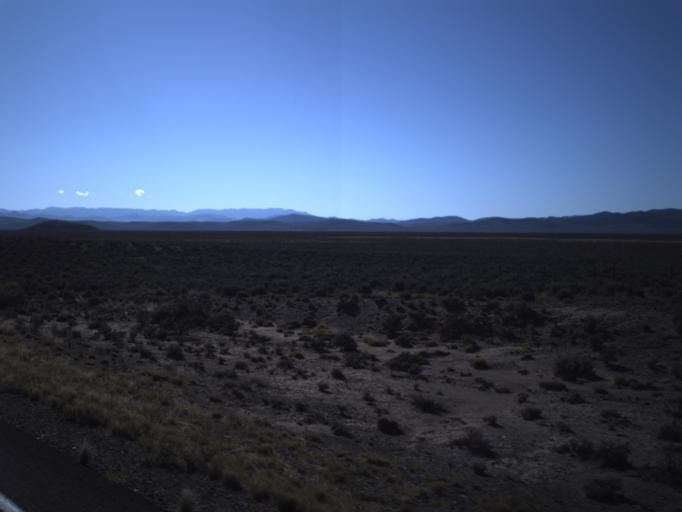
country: US
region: Utah
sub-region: Washington County
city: Enterprise
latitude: 37.7871
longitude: -113.8776
